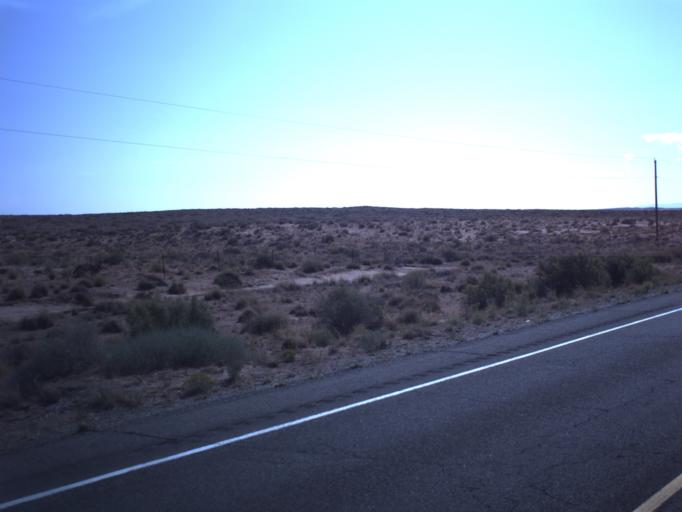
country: US
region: Utah
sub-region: San Juan County
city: Blanding
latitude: 37.1340
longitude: -109.5534
